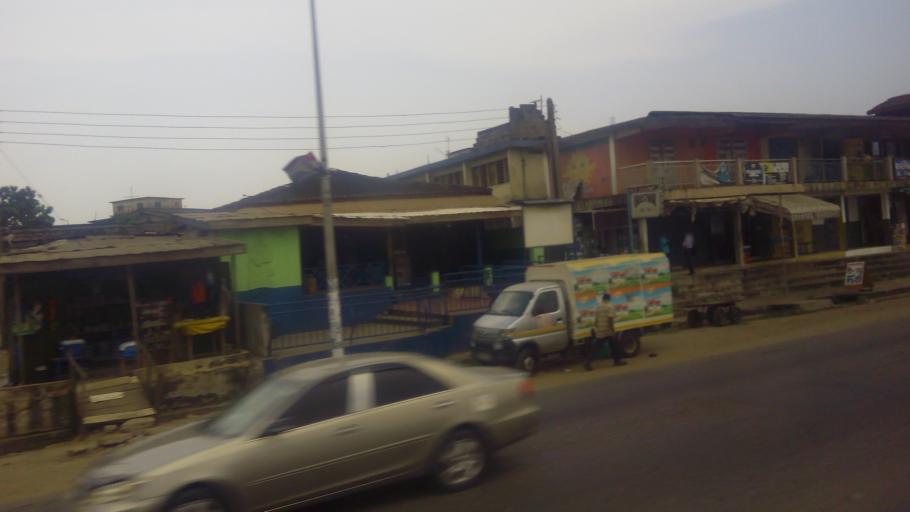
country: GH
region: Western
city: Takoradi
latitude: 4.8996
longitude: -1.7666
